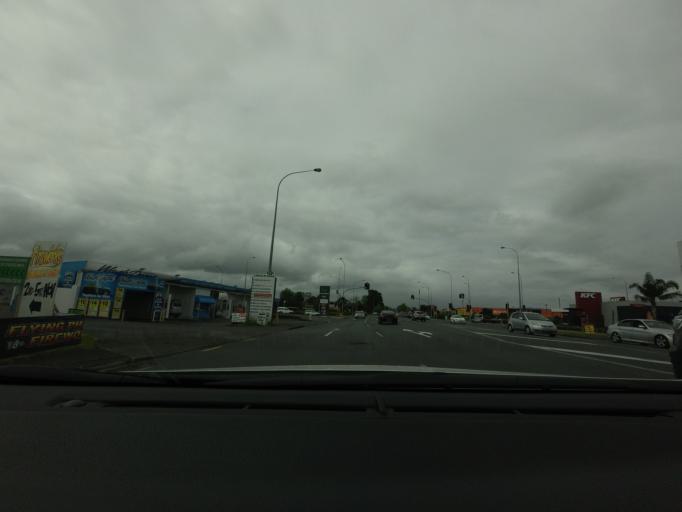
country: NZ
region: Auckland
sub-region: Auckland
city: Rosebank
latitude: -36.8563
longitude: 174.6301
